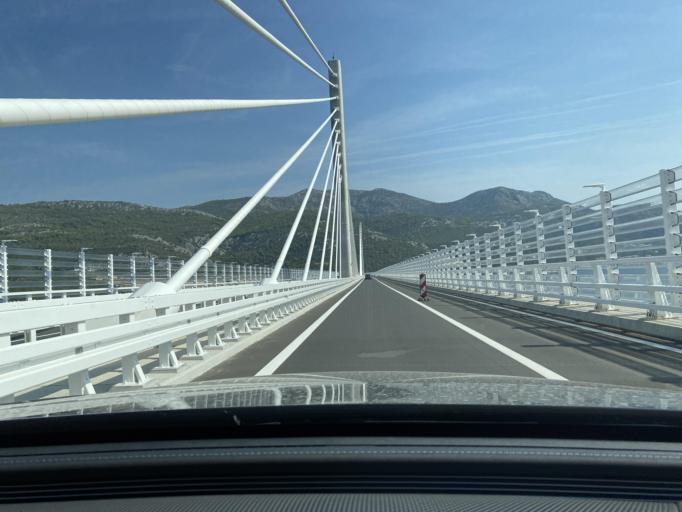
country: BA
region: Federation of Bosnia and Herzegovina
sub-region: Hercegovacko-Bosanski Kanton
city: Neum
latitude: 42.9340
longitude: 17.5383
